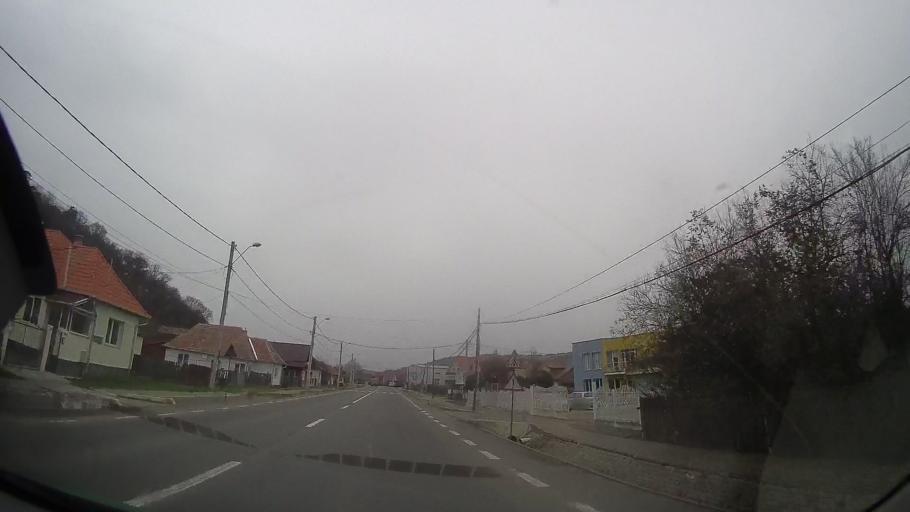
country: RO
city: Remetea
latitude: 46.5979
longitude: 24.5312
